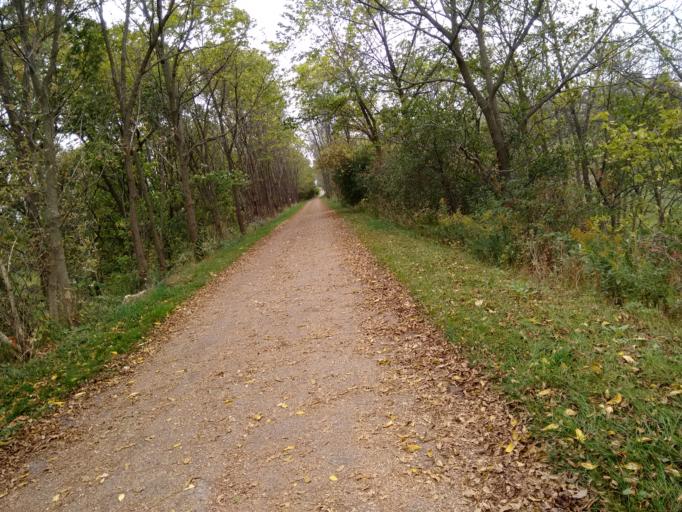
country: CA
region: Ontario
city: Stratford
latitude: 43.2632
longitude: -81.1493
